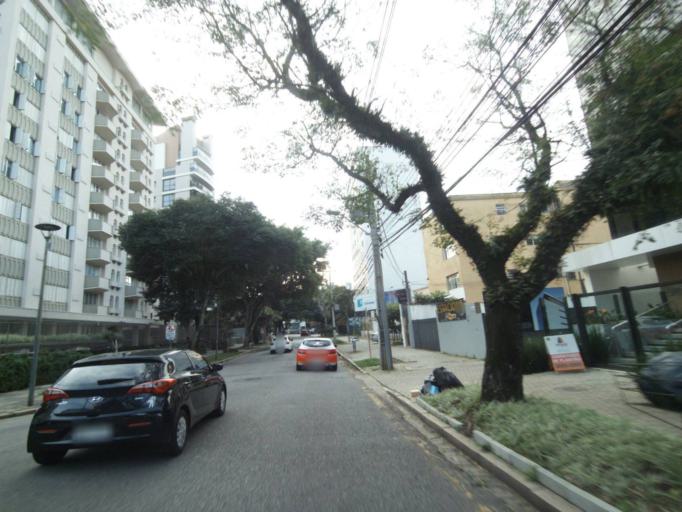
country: BR
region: Parana
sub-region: Curitiba
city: Curitiba
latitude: -25.4375
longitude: -49.2848
